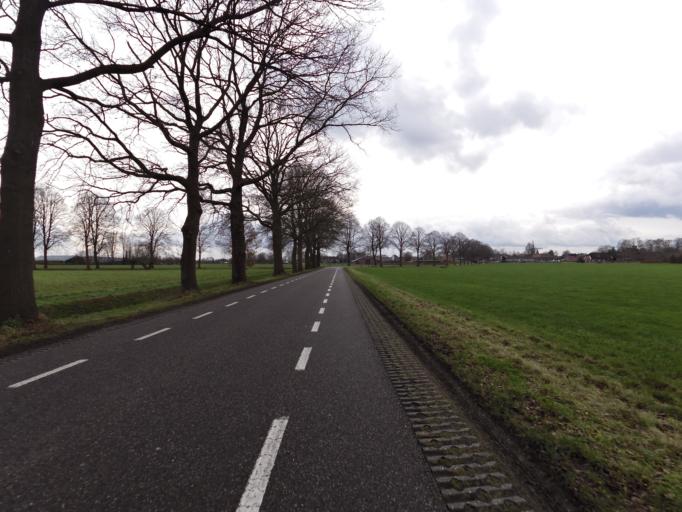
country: NL
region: Gelderland
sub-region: Oude IJsselstreek
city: Wisch
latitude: 51.9145
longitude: 6.3985
